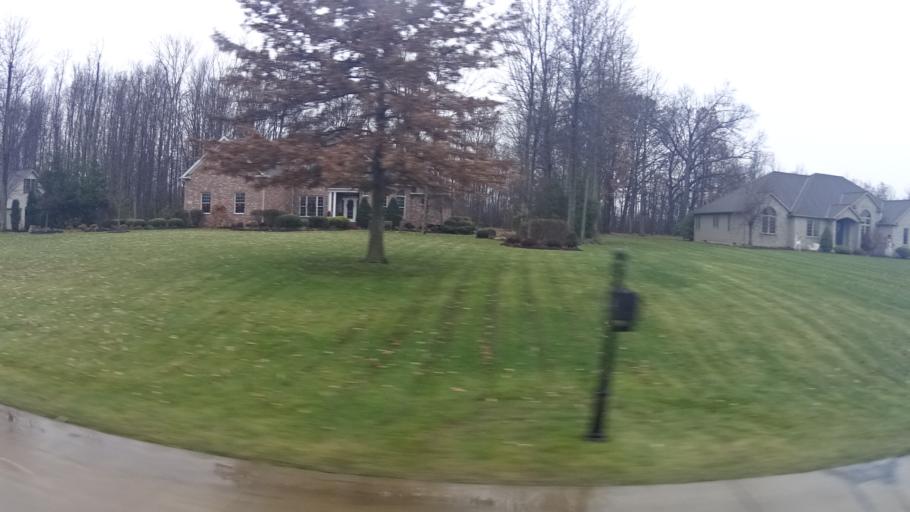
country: US
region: Ohio
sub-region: Lorain County
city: Lagrange
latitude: 41.2950
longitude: -82.1292
